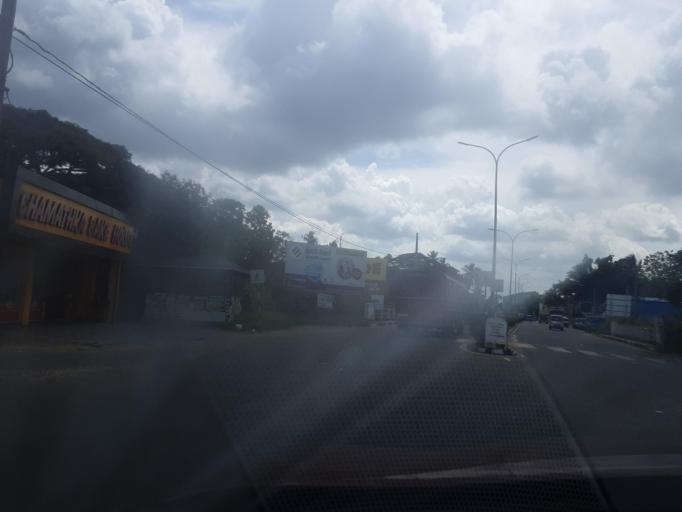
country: LK
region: North Western
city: Kuliyapitiya
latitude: 7.4692
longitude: 80.0304
